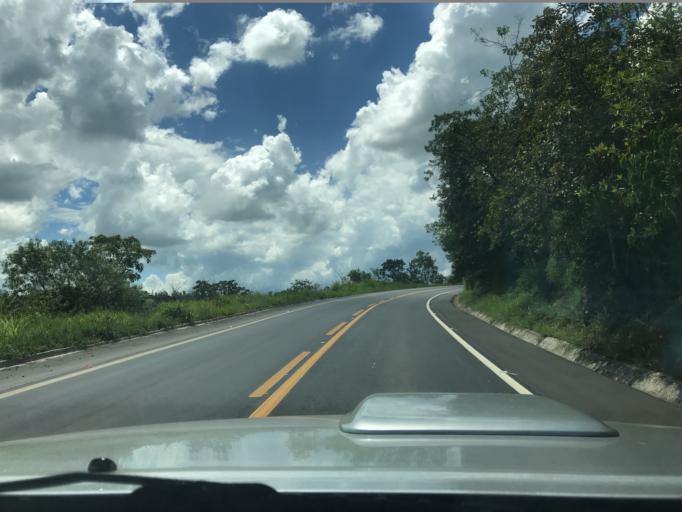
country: BR
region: Minas Gerais
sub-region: Formiga
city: Formiga
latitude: -20.6416
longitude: -45.3640
